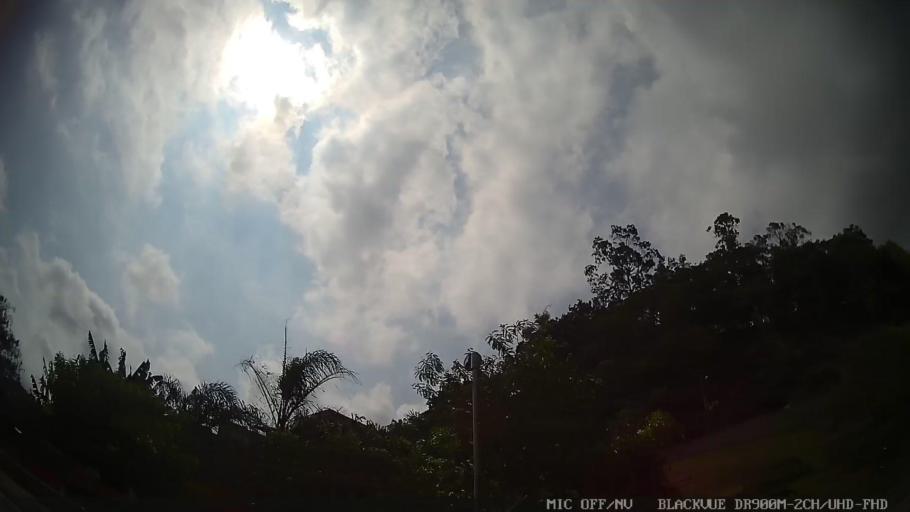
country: BR
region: Sao Paulo
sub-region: Taboao Da Serra
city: Taboao da Serra
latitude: -23.6647
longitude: -46.7314
